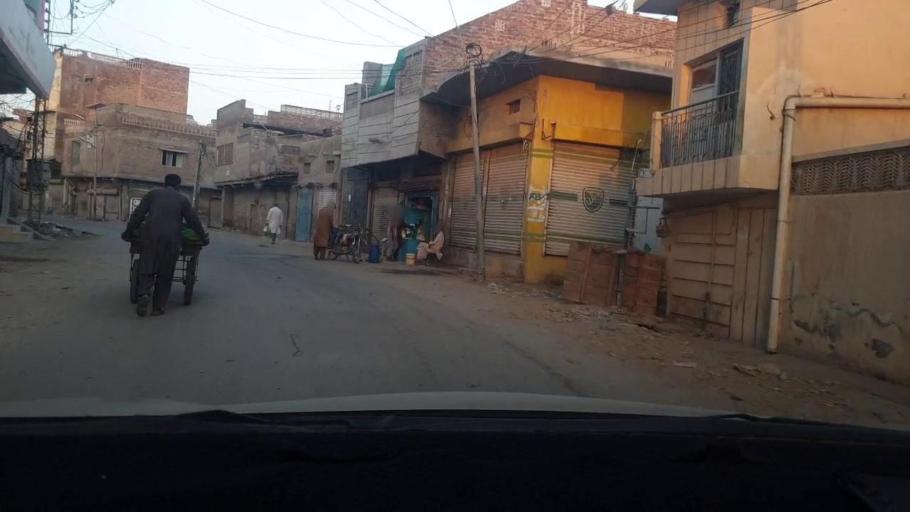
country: PK
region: Sindh
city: Larkana
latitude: 27.5593
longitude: 68.2181
